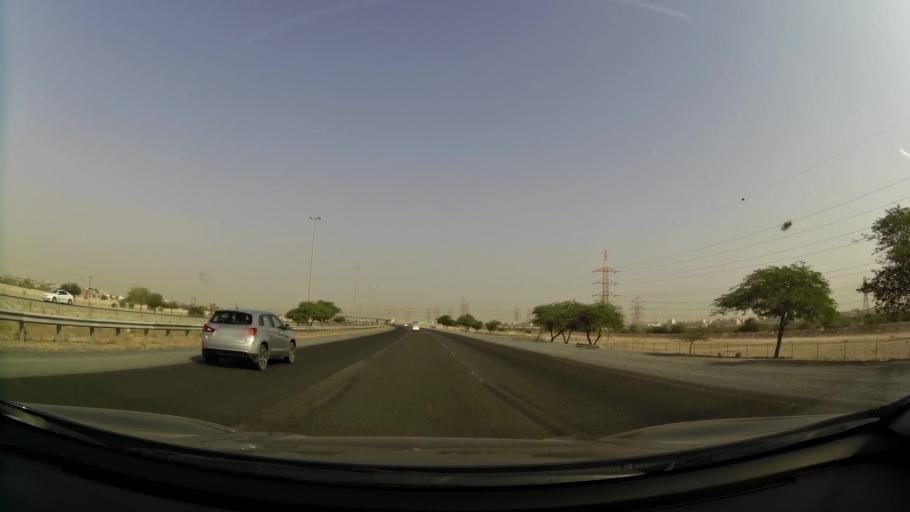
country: KW
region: Al Asimah
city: Ar Rabiyah
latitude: 29.2285
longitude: 47.8852
